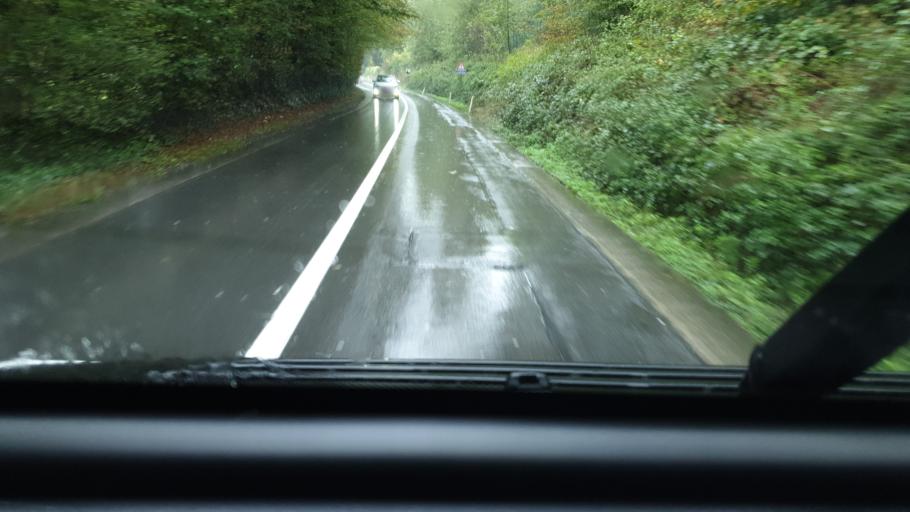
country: BE
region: Wallonia
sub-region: Province du Hainaut
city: Charleroi
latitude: 50.3693
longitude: 4.4775
